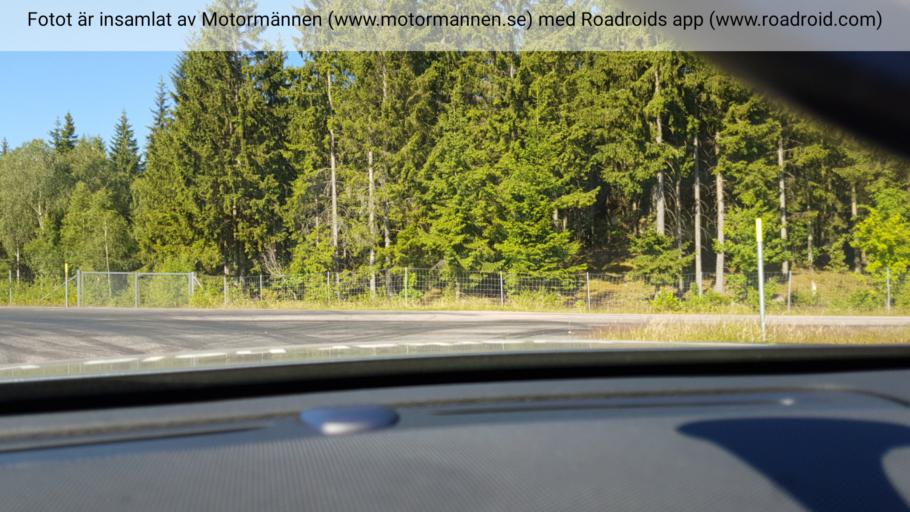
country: SE
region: Kronoberg
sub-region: Markaryds Kommun
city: Stromsnasbruk
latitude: 56.6165
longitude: 13.7597
